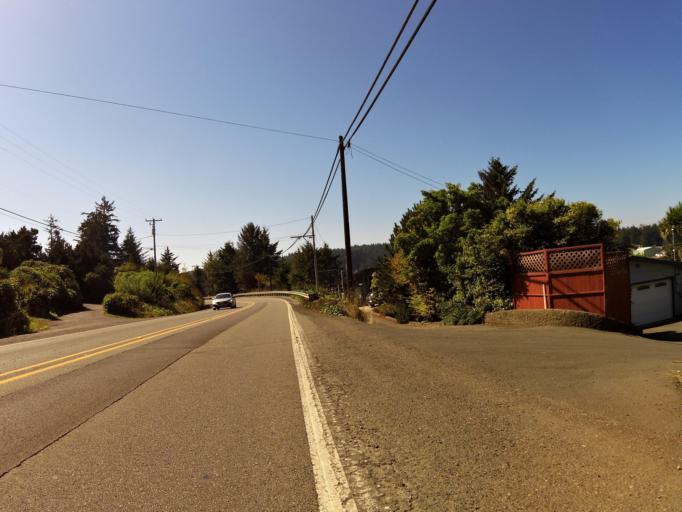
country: US
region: Oregon
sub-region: Coos County
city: Barview
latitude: 43.3414
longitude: -124.3164
